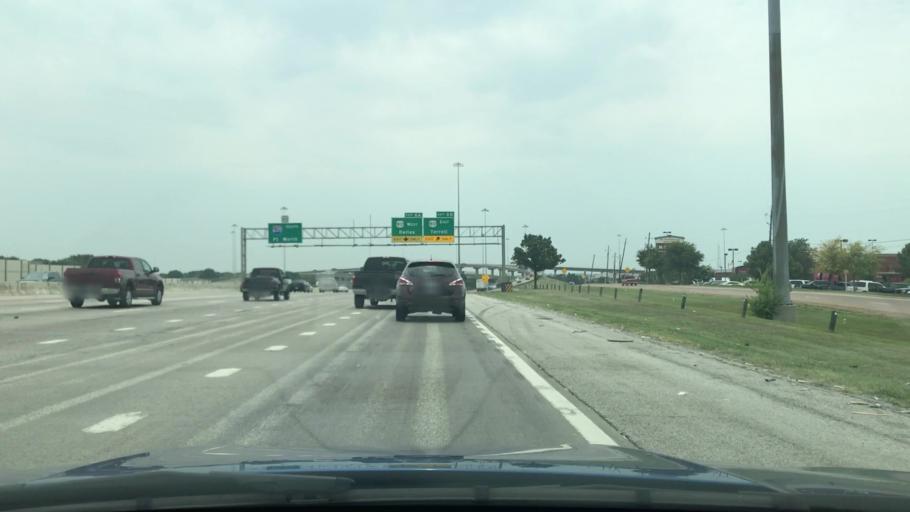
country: US
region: Texas
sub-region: Dallas County
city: Mesquite
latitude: 32.7990
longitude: -96.6263
